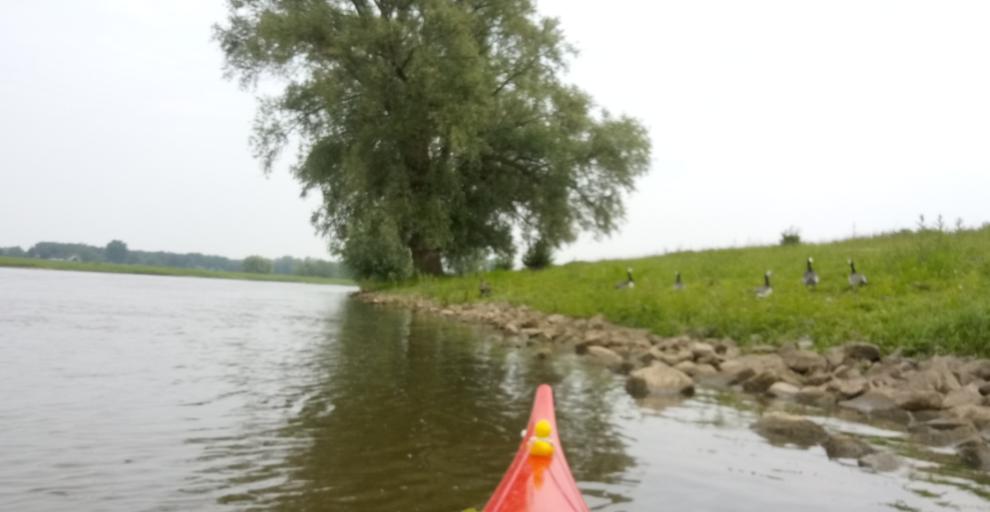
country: NL
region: Gelderland
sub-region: Gemeente Lochem
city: Gorssel
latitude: 52.1794
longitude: 6.1880
